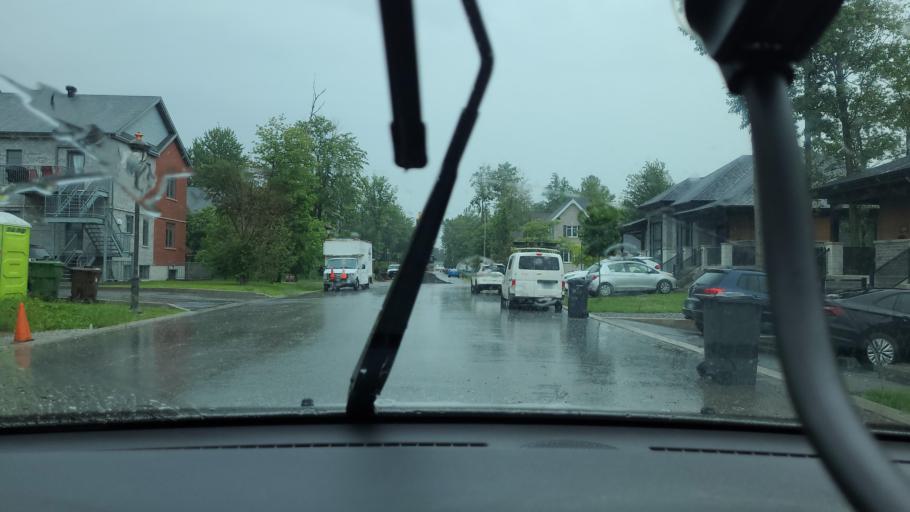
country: CA
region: Quebec
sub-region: Monteregie
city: Saint-Hyacinthe
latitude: 45.6124
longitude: -72.9862
